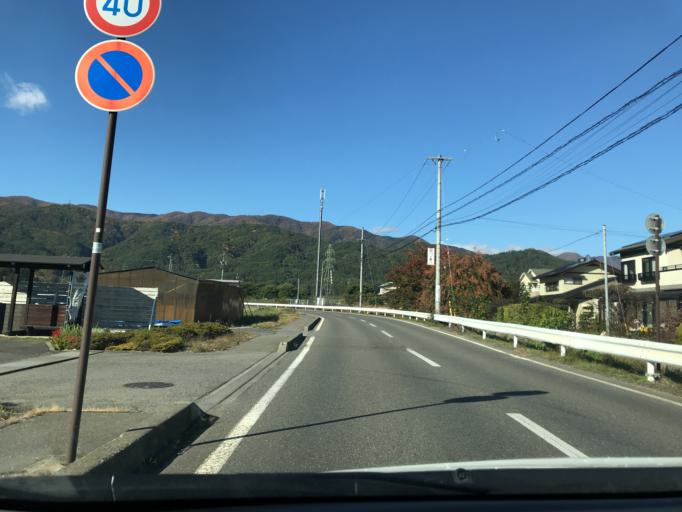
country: JP
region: Nagano
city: Matsumoto
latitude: 36.1716
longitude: 137.8775
